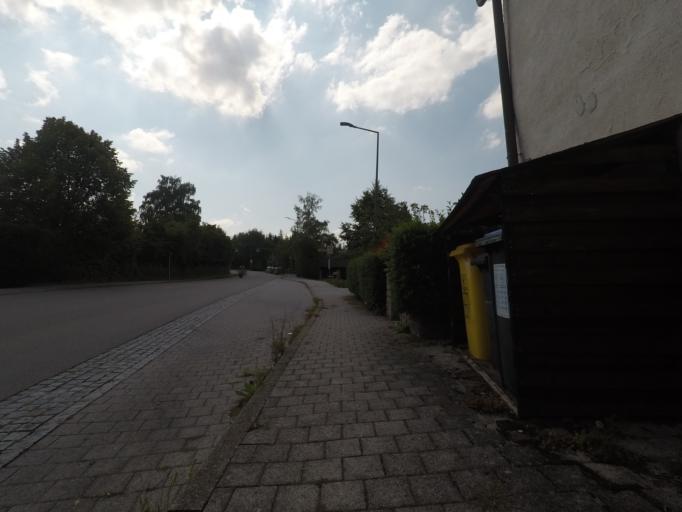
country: DE
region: Baden-Wuerttemberg
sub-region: Regierungsbezirk Stuttgart
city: Winterbach
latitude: 48.7902
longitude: 9.4656
